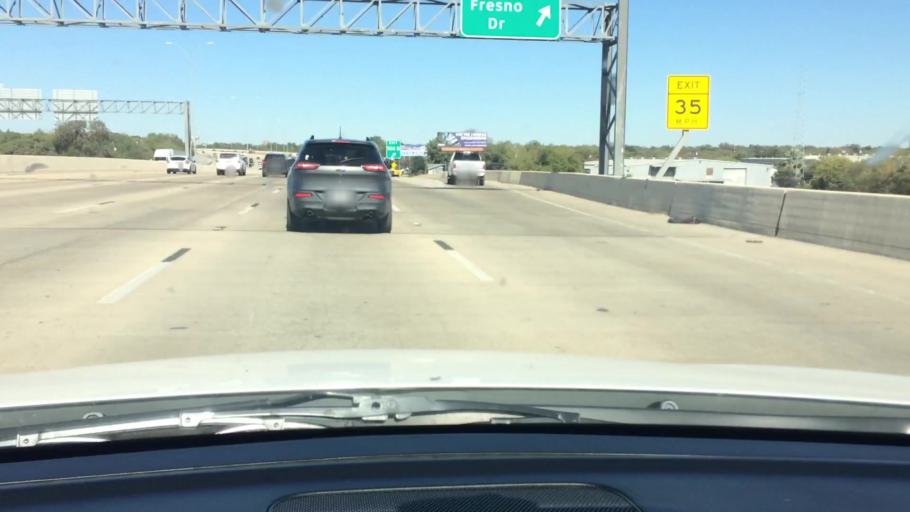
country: US
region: Texas
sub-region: Bexar County
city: Olmos Park
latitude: 29.4669
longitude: -98.5158
